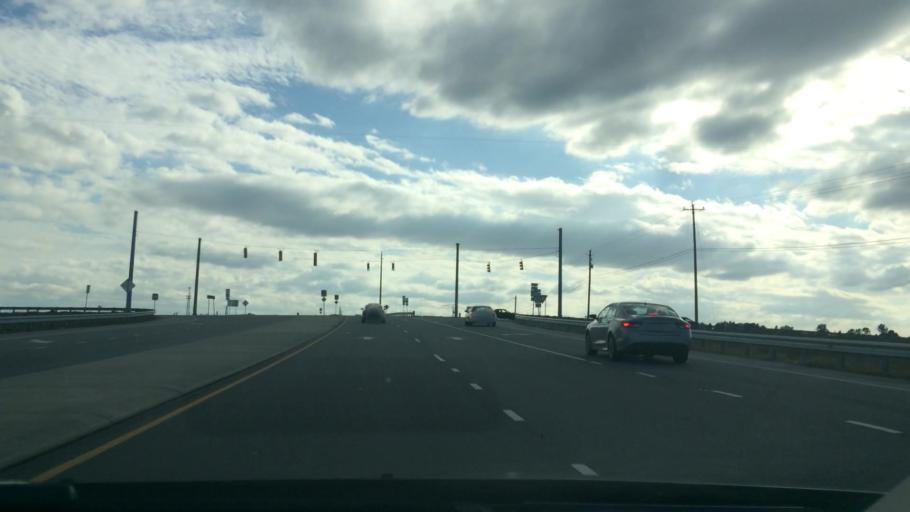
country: US
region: North Carolina
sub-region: Wayne County
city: Elroy
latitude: 35.4141
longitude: -77.8967
